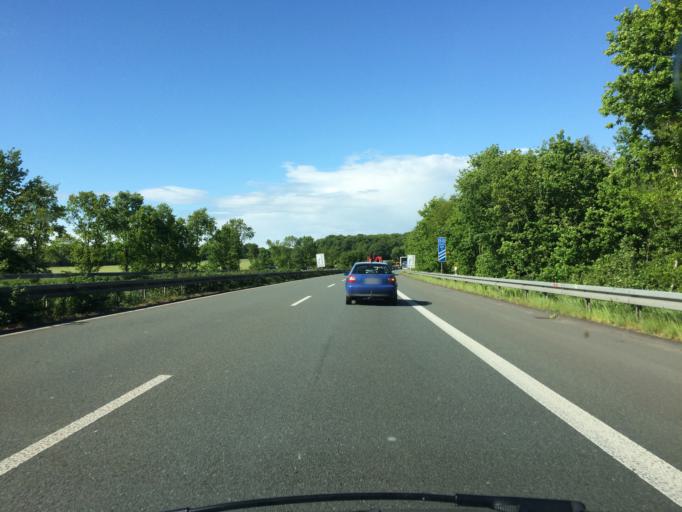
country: DE
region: North Rhine-Westphalia
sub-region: Regierungsbezirk Munster
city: Haltern
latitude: 51.6968
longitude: 7.1395
